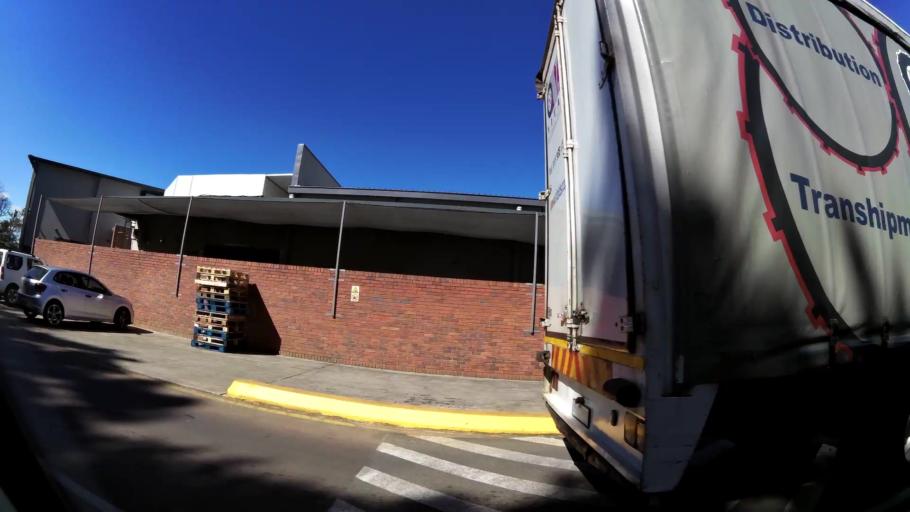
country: ZA
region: Limpopo
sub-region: Mopani District Municipality
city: Tzaneen
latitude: -23.8217
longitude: 30.1573
